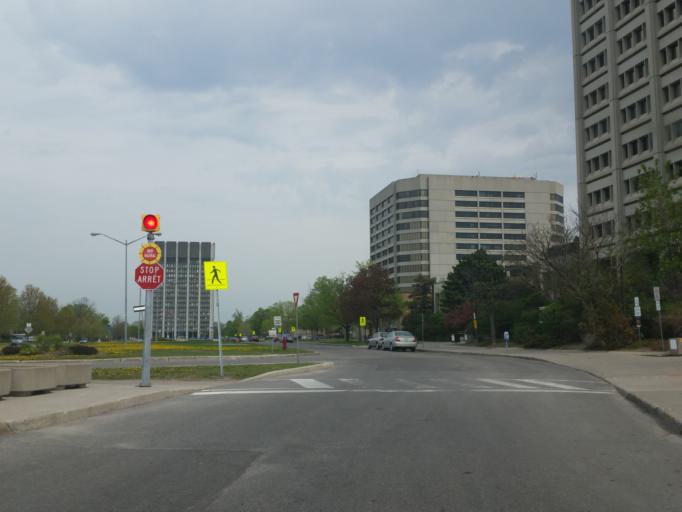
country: CA
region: Ontario
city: Ottawa
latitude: 45.4043
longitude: -75.7346
